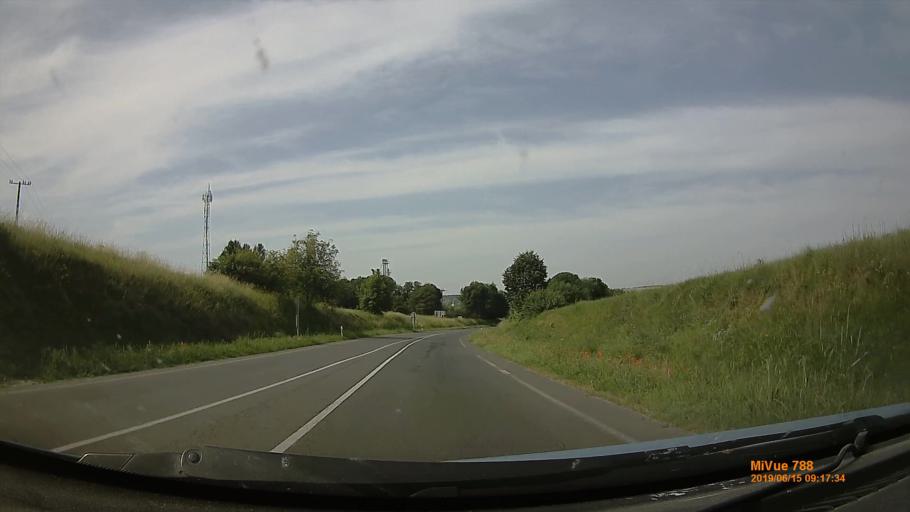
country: HU
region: Tolna
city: Tamasi
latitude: 46.6040
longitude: 18.2069
